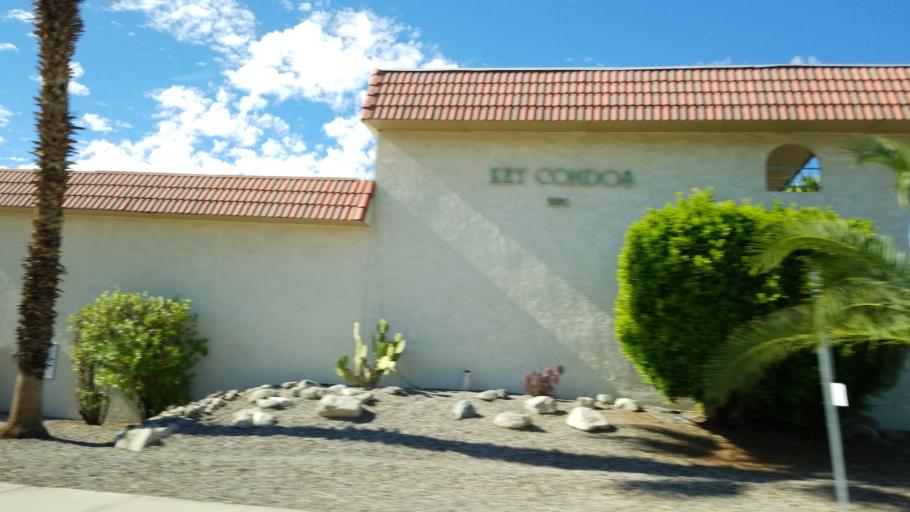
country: US
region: Arizona
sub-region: Mohave County
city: Lake Havasu City
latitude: 34.4777
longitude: -114.3198
